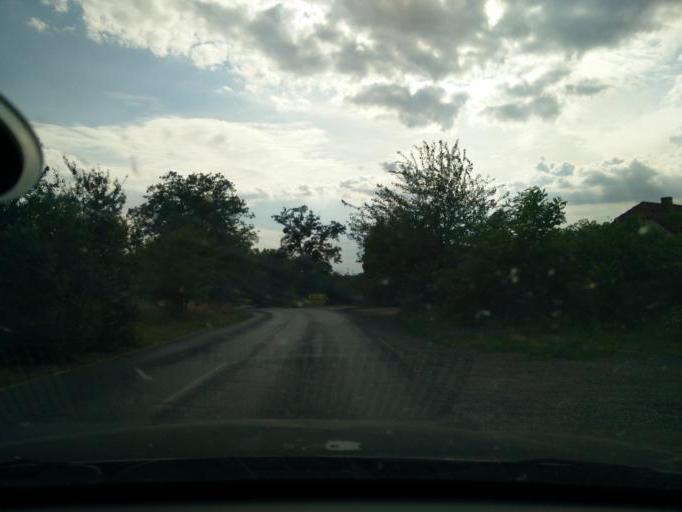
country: HU
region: Komarom-Esztergom
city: Baj
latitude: 47.6602
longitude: 18.3490
